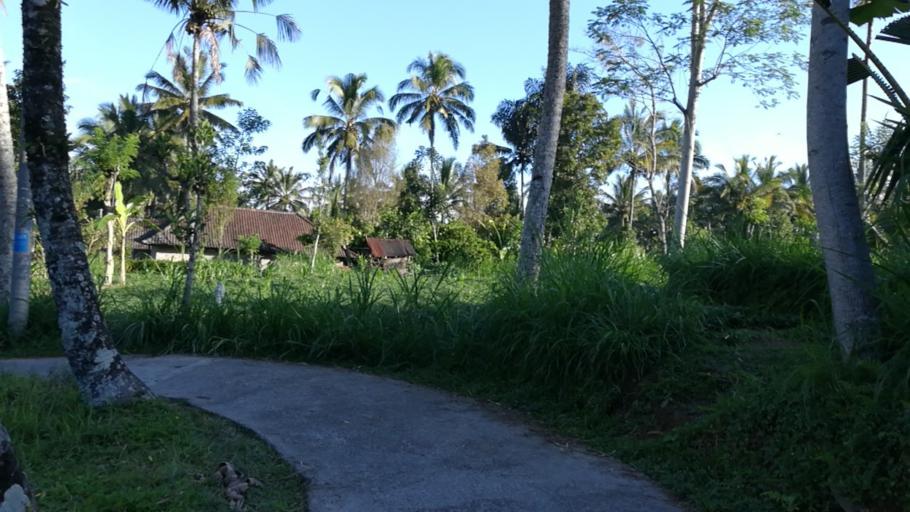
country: ID
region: Bali
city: Banjar Wangsian
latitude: -8.4344
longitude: 115.4293
